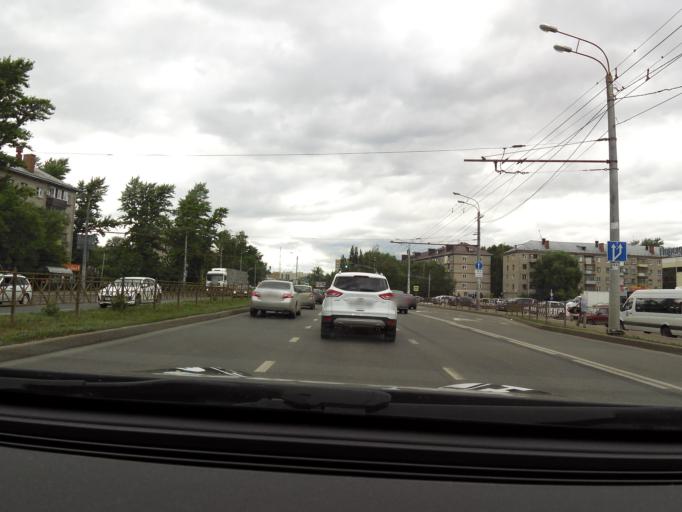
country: RU
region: Tatarstan
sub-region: Gorod Kazan'
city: Kazan
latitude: 55.8170
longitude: 49.0645
